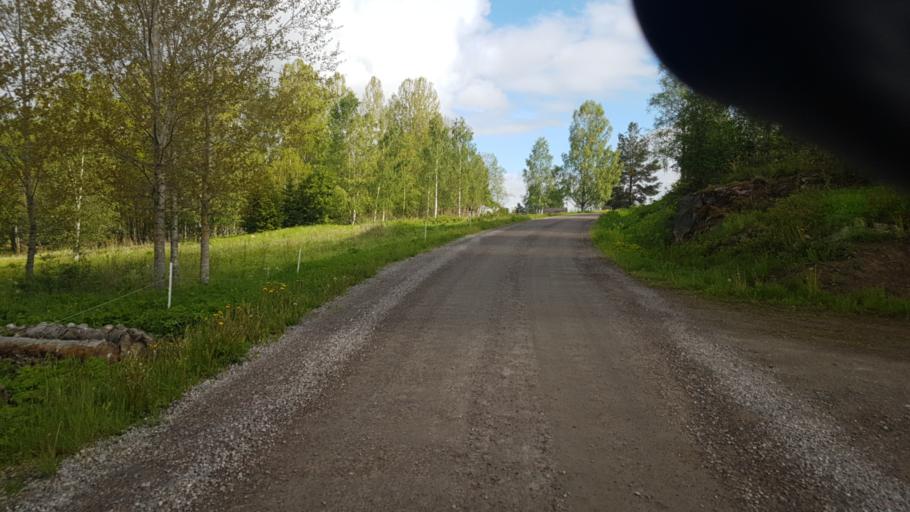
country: NO
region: Ostfold
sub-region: Romskog
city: Romskog
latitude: 59.8549
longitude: 11.9653
